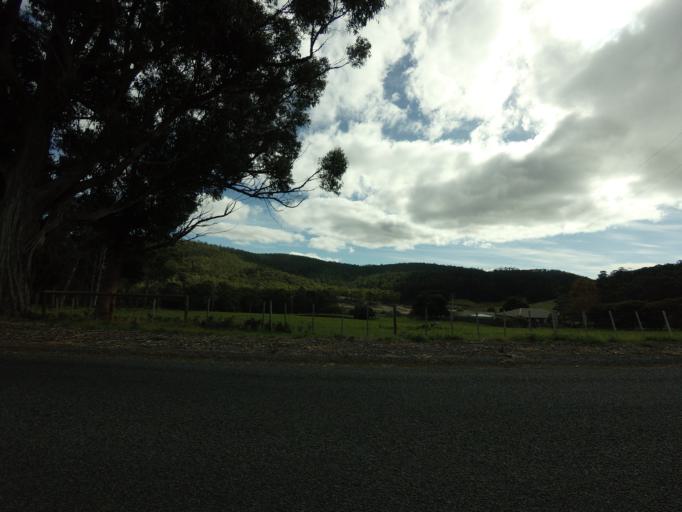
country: AU
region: Tasmania
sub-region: Clarence
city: Sandford
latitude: -43.0809
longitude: 147.7397
